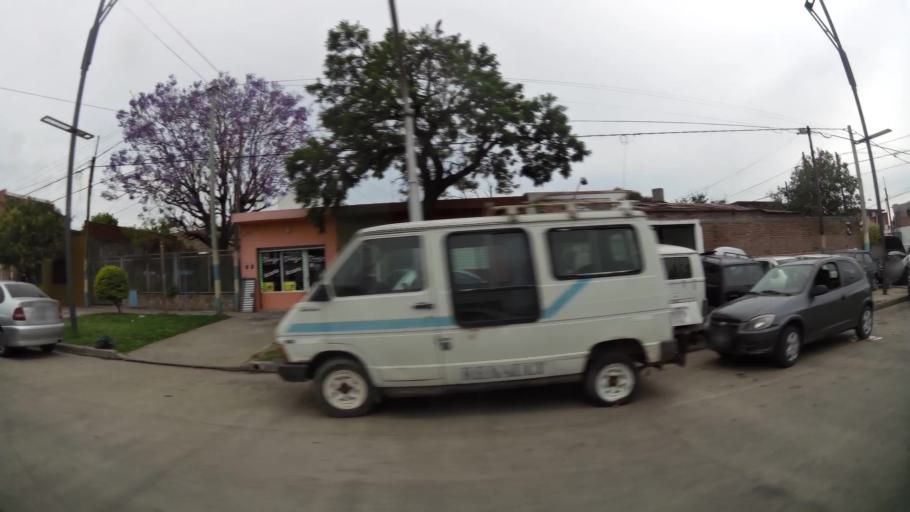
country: AR
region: Santa Fe
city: Granadero Baigorria
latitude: -32.9000
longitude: -60.7057
